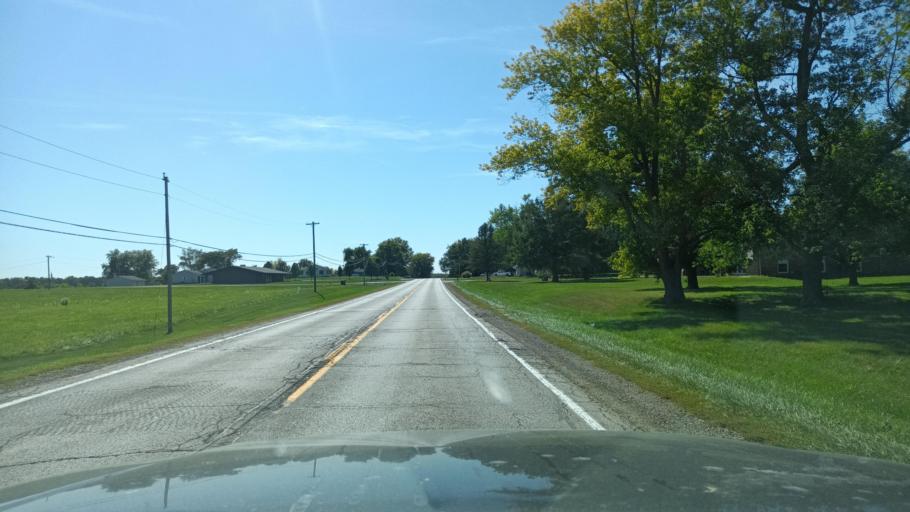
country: US
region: Illinois
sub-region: De Witt County
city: Farmer City
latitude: 40.2372
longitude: -88.6517
